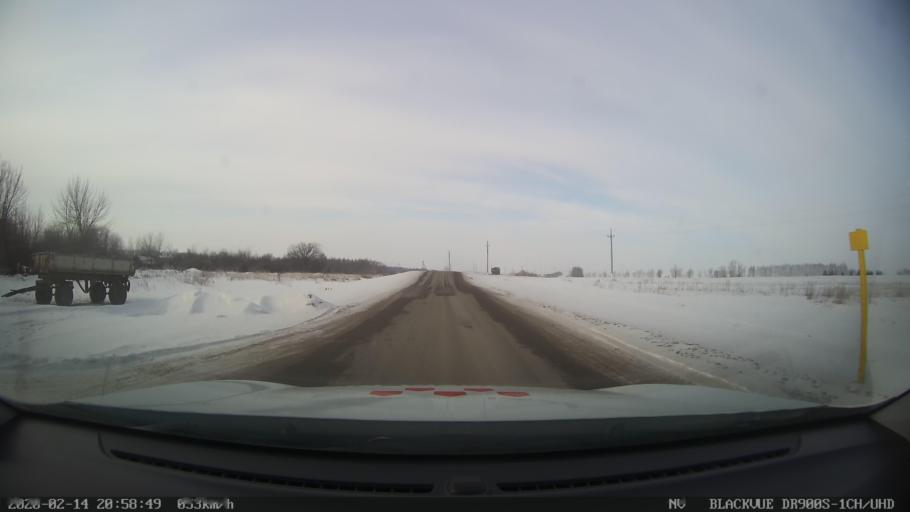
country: RU
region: Tatarstan
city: Kuybyshevskiy Zaton
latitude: 55.1786
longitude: 49.2448
